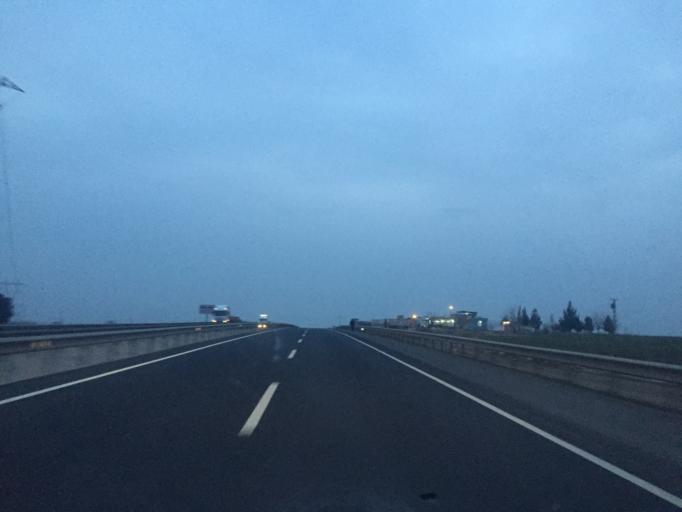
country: TR
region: Sanliurfa
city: Camlidere
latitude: 37.1579
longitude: 39.0408
